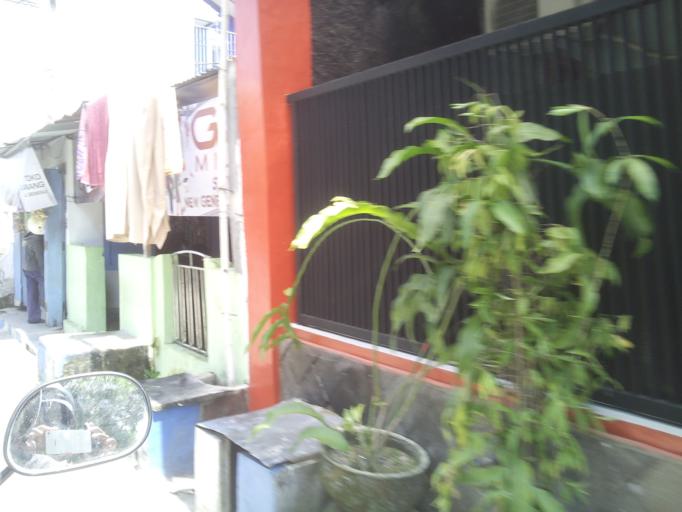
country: ID
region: East Java
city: Sumbersari Wetan
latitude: -8.1792
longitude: 113.7206
